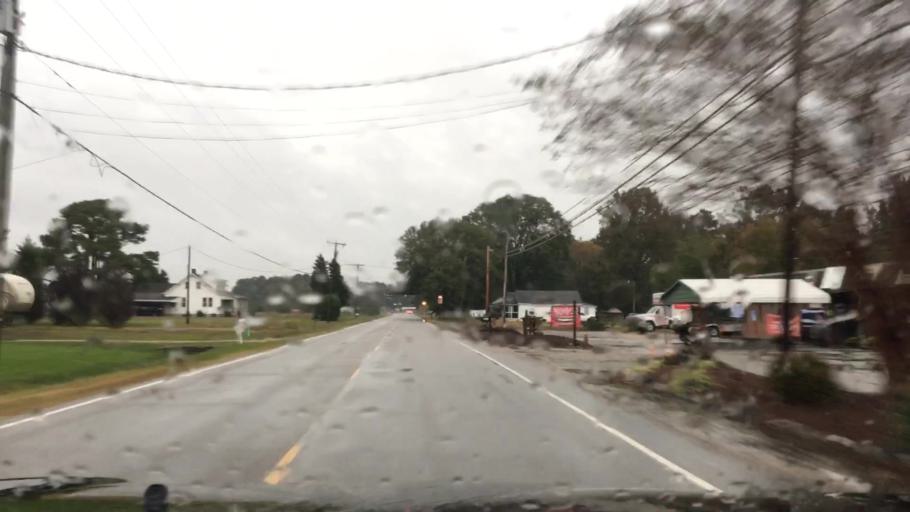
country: US
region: North Carolina
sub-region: Currituck County
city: Moyock
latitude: 36.6712
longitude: -76.2268
